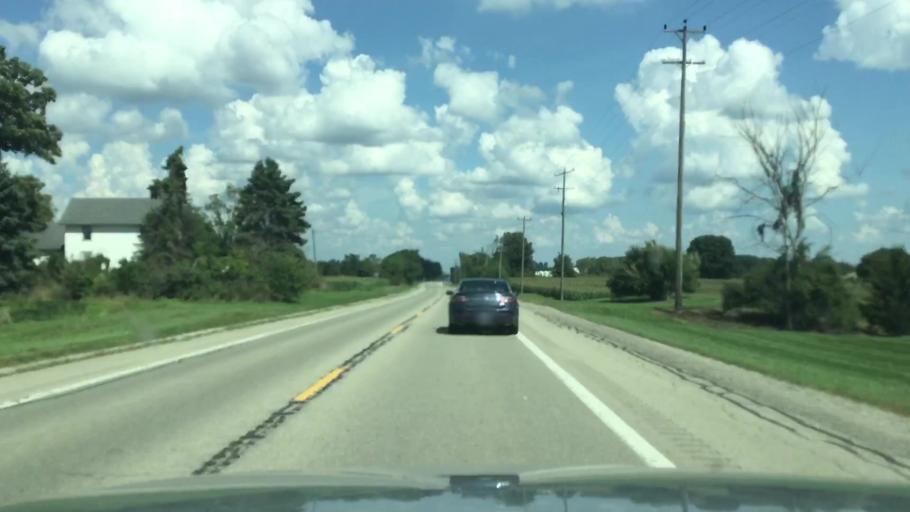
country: US
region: Michigan
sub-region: Washtenaw County
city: Saline
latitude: 42.1448
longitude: -83.8338
